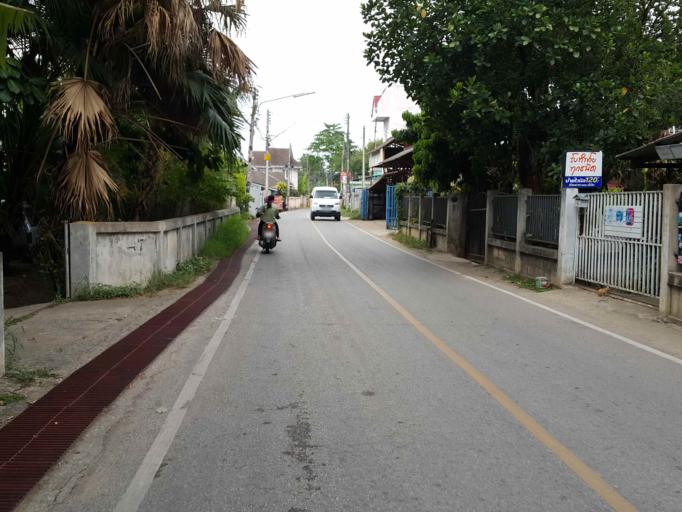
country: TH
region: Chiang Mai
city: Chiang Mai
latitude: 18.7547
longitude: 98.9982
